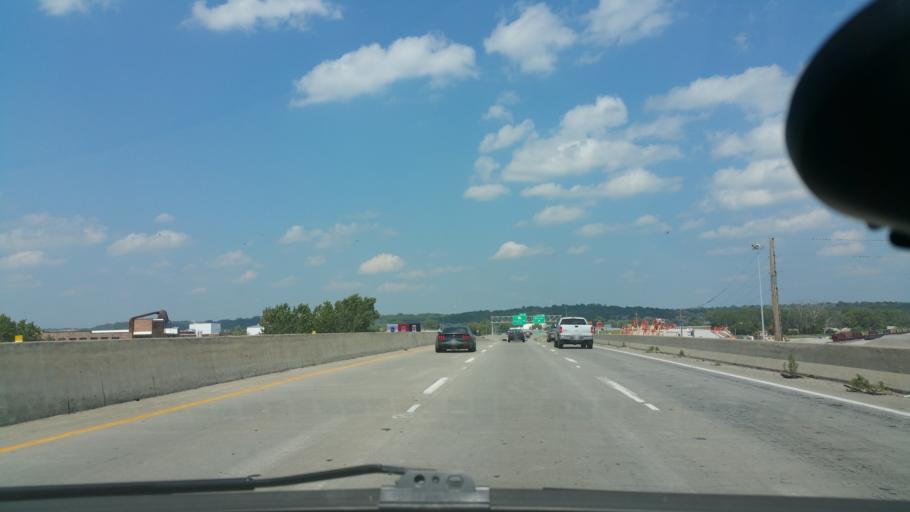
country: US
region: Missouri
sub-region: Clay County
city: North Kansas City
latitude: 39.1322
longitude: -94.5679
